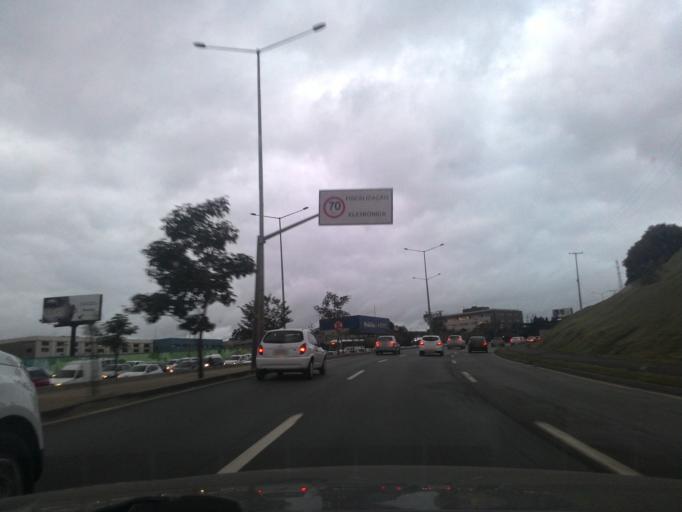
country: BR
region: Parana
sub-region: Curitiba
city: Curitiba
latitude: -25.4558
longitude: -49.2484
